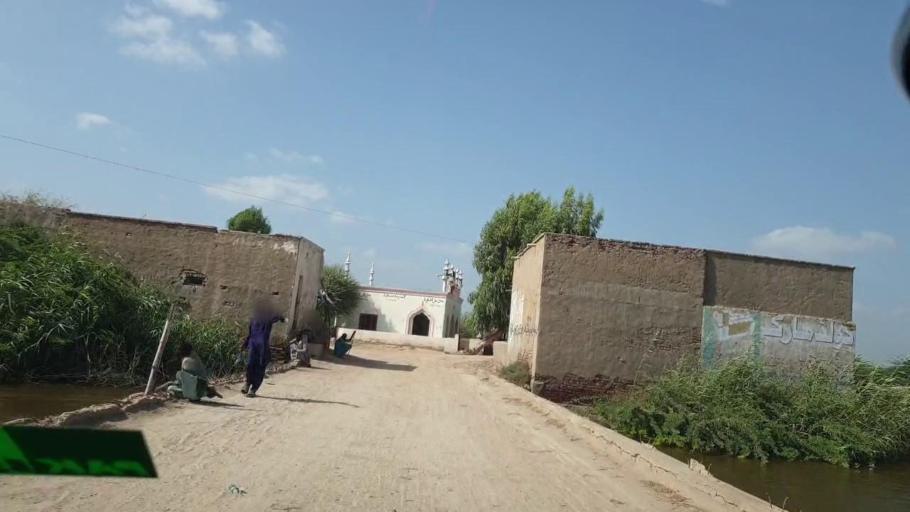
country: PK
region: Sindh
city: Tando Bago
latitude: 24.6752
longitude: 69.1953
